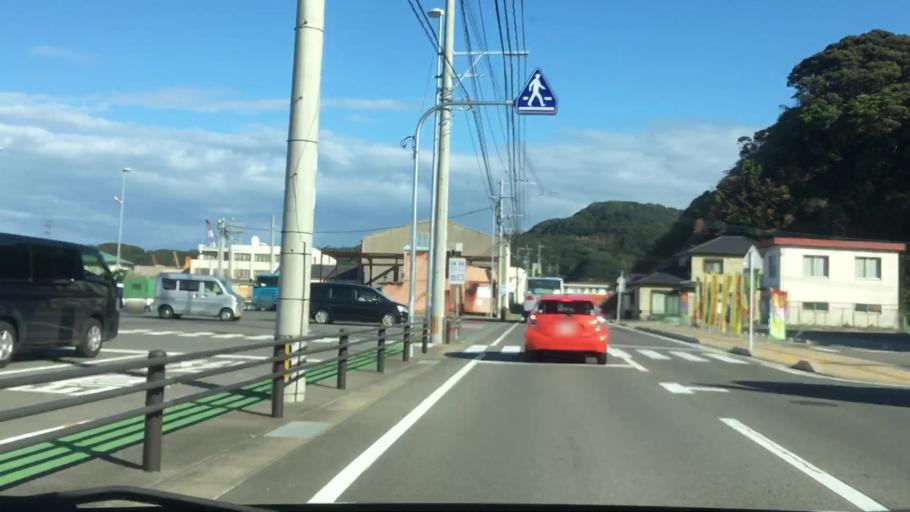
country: JP
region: Nagasaki
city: Sasebo
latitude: 32.9404
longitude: 129.6392
